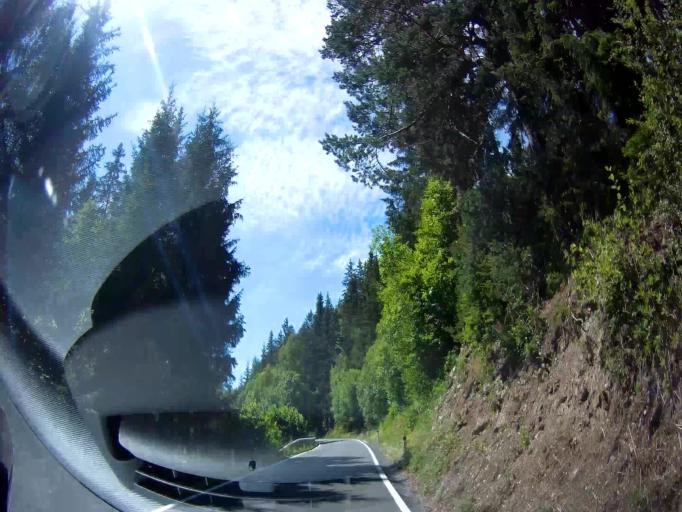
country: AT
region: Carinthia
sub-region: Politischer Bezirk Sankt Veit an der Glan
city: Glodnitz
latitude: 46.9157
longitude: 14.0732
